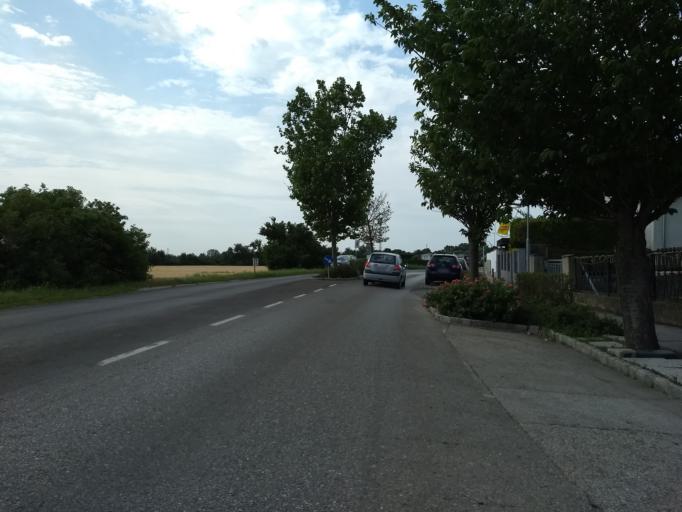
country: AT
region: Lower Austria
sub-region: Politischer Bezirk Modling
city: Neu-Guntramsdorf
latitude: 48.0552
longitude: 16.3231
